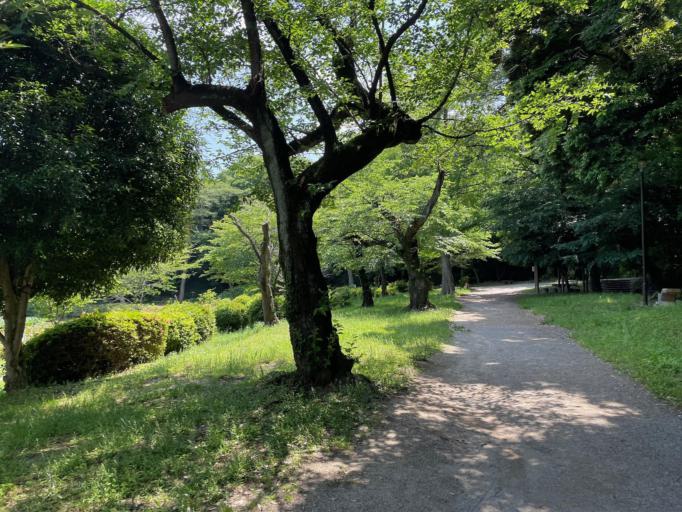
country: JP
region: Saitama
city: Iwatsuki
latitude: 35.9515
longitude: 139.7114
